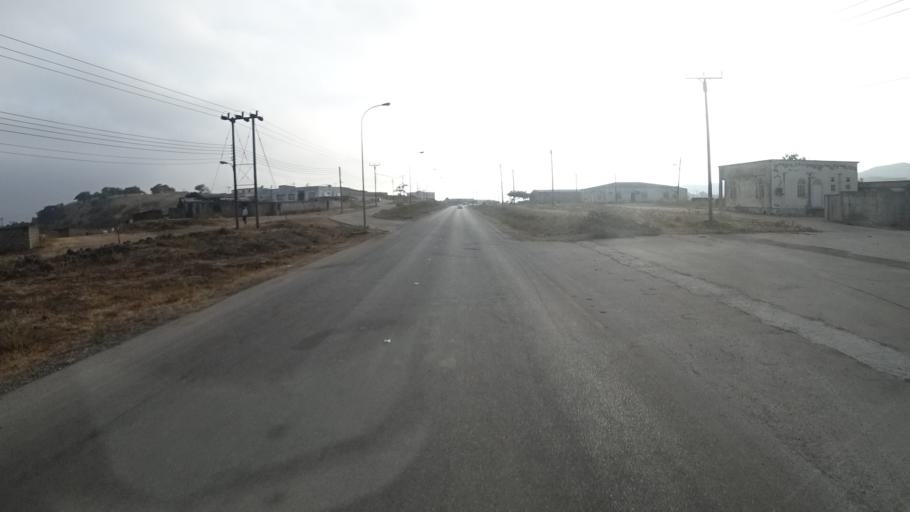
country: OM
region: Zufar
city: Salalah
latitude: 17.1207
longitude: 53.9908
